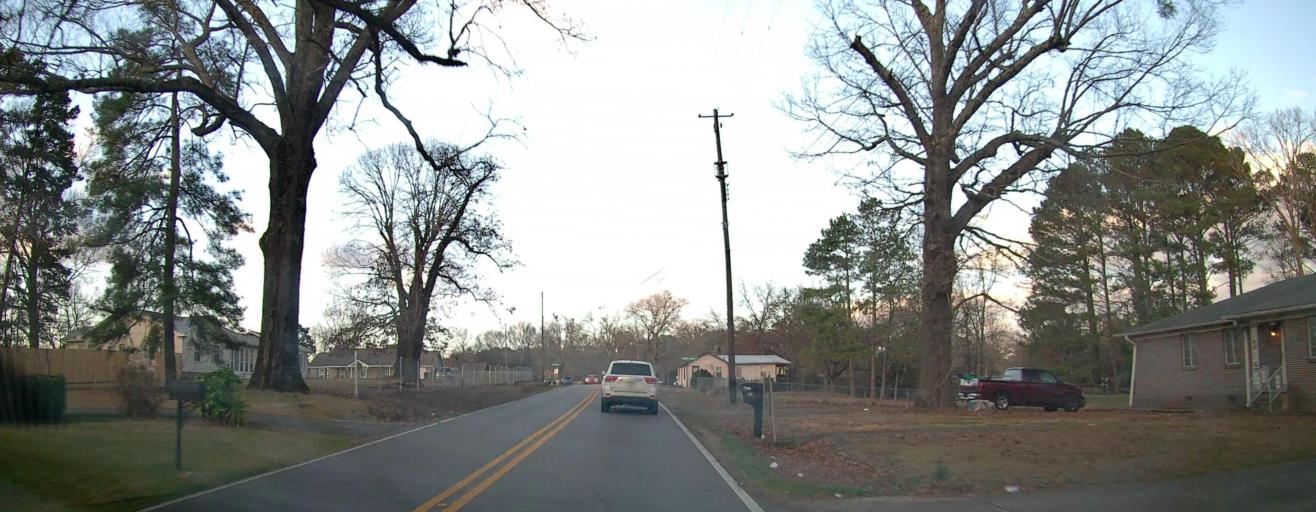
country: US
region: Alabama
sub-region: Etowah County
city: Gadsden
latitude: 33.9861
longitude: -85.9864
